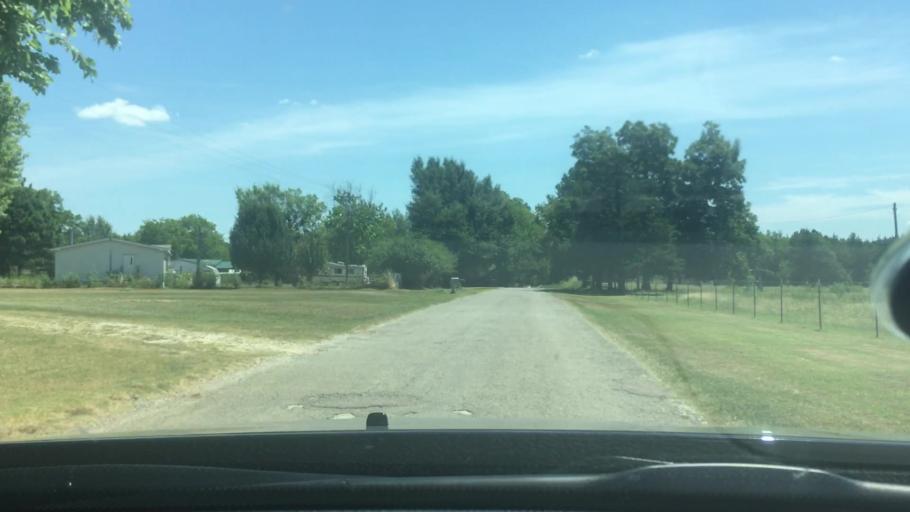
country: US
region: Oklahoma
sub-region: Bryan County
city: Durant
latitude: 33.9830
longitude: -96.2546
